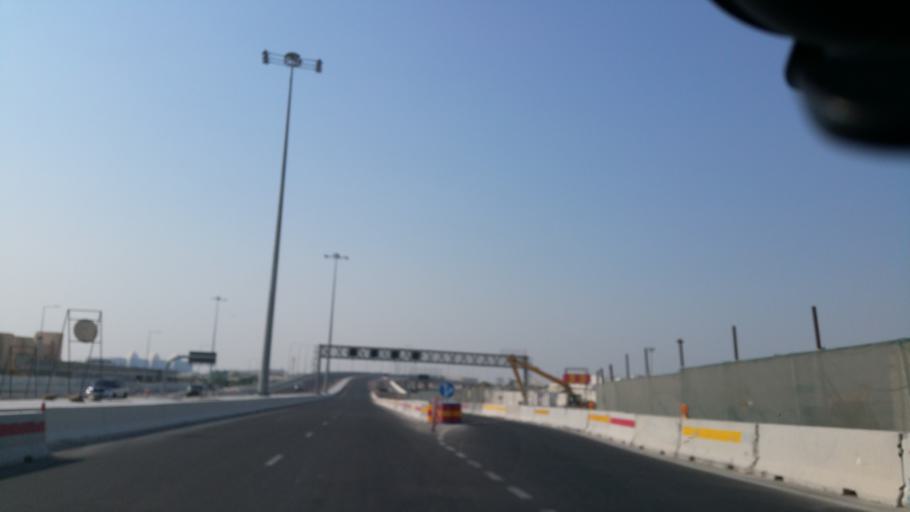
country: QA
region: Baladiyat ar Rayyan
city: Ar Rayyan
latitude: 25.3077
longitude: 51.4634
